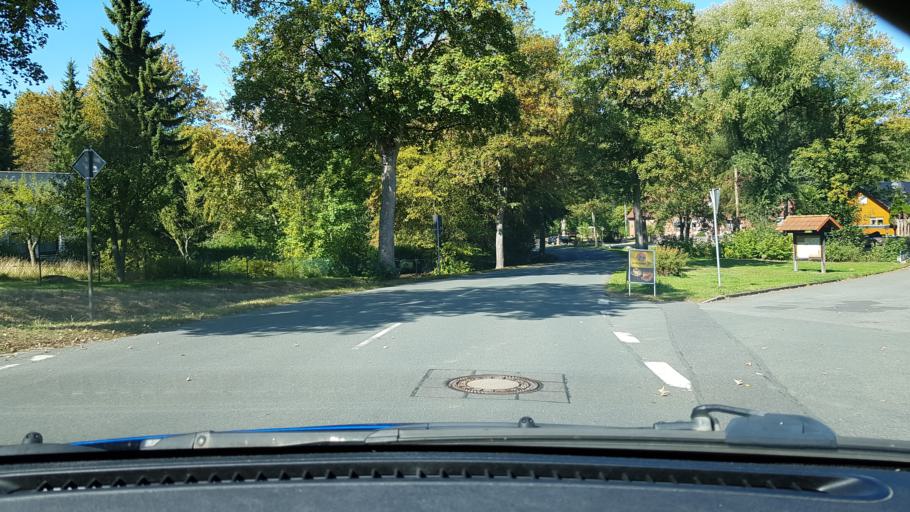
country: DE
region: Lower Saxony
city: Barsinghausen
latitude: 52.2592
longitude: 9.4420
